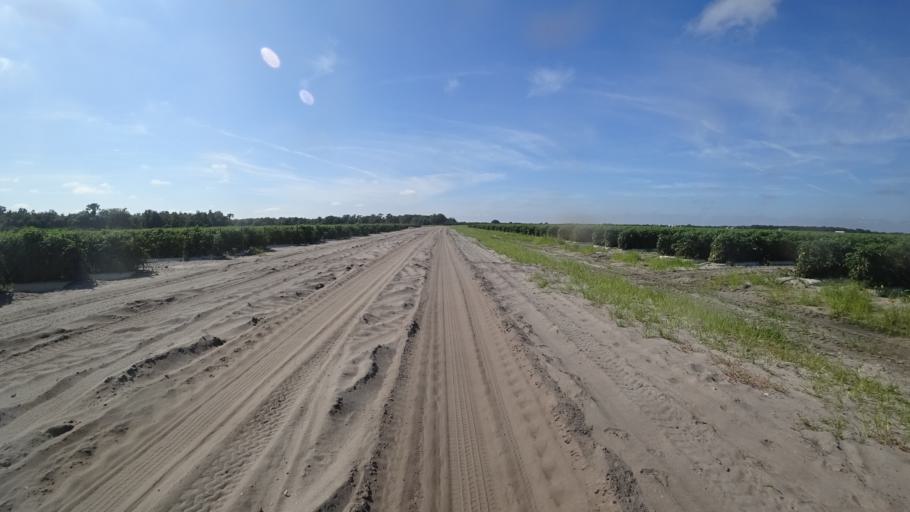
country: US
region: Florida
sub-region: DeSoto County
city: Arcadia
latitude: 27.2947
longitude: -82.0479
